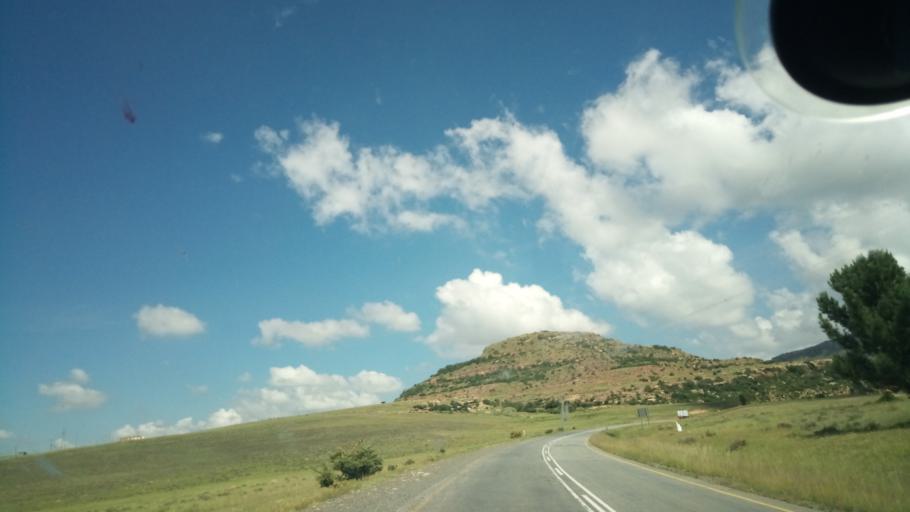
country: ZA
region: Orange Free State
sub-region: Thabo Mofutsanyana District Municipality
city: Ficksburg
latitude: -28.8935
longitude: 27.8481
